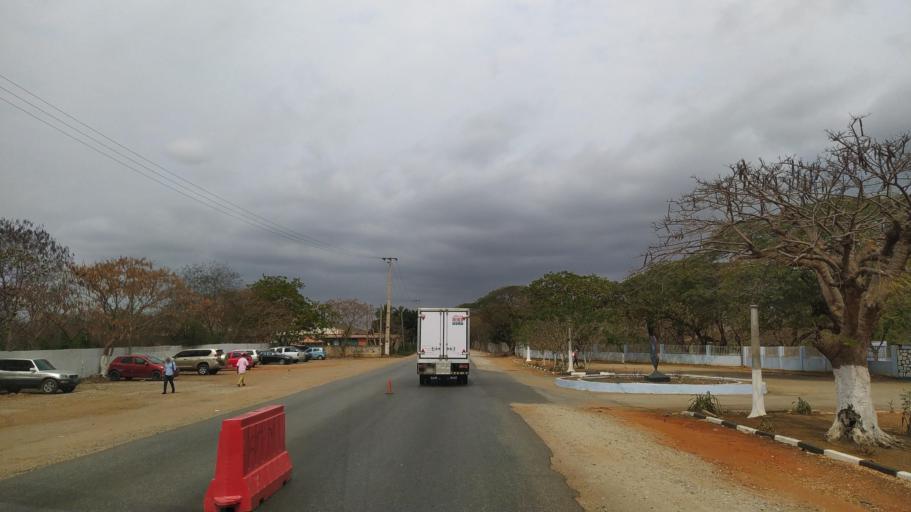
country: AO
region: Luanda
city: Luanda
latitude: -8.8576
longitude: 13.2862
